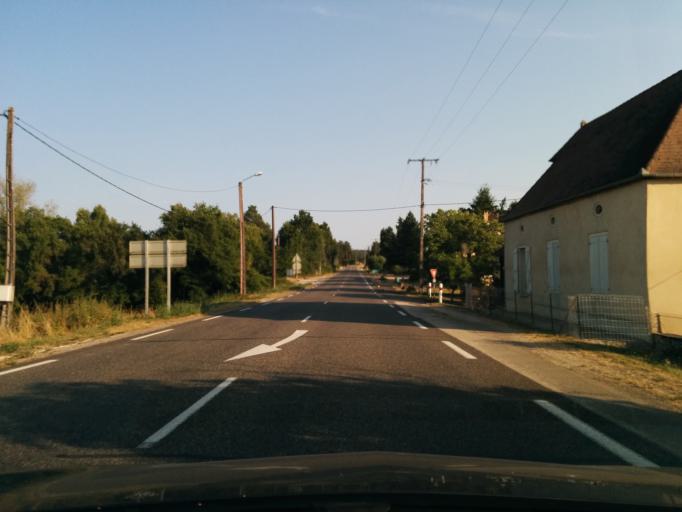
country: FR
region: Midi-Pyrenees
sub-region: Departement du Lot
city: Le Vigan
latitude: 44.7842
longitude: 1.4683
